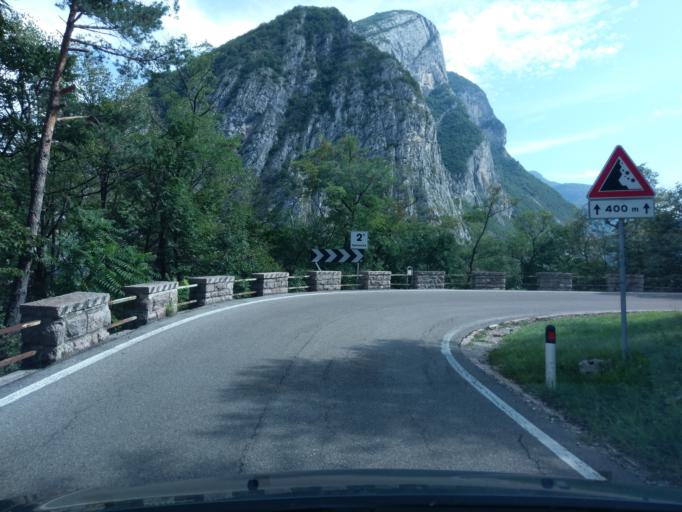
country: IT
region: Trentino-Alto Adige
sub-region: Provincia di Trento
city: Spormaggiore
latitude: 46.2335
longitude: 11.0597
